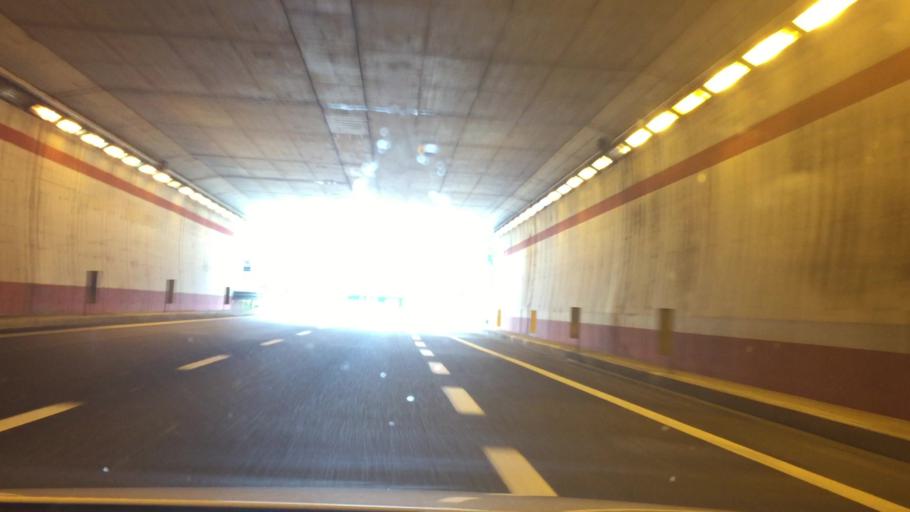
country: IT
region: Lombardy
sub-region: Provincia di Varese
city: Lonate Pozzolo
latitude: 45.5734
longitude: 8.7392
